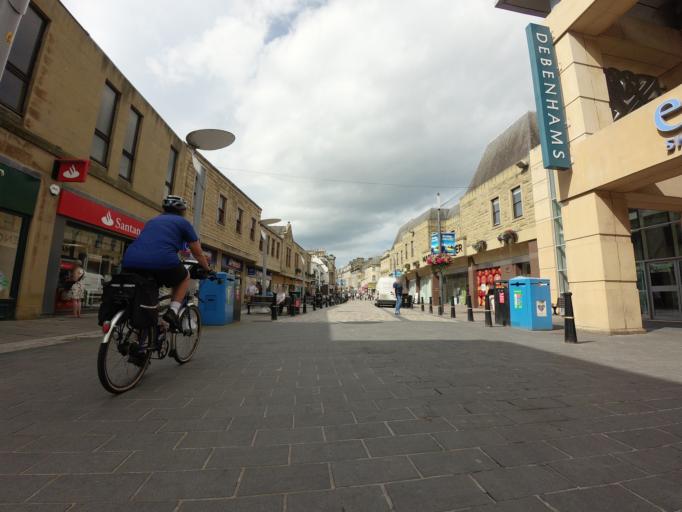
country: GB
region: Scotland
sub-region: Highland
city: Inverness
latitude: 57.4783
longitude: -4.2215
